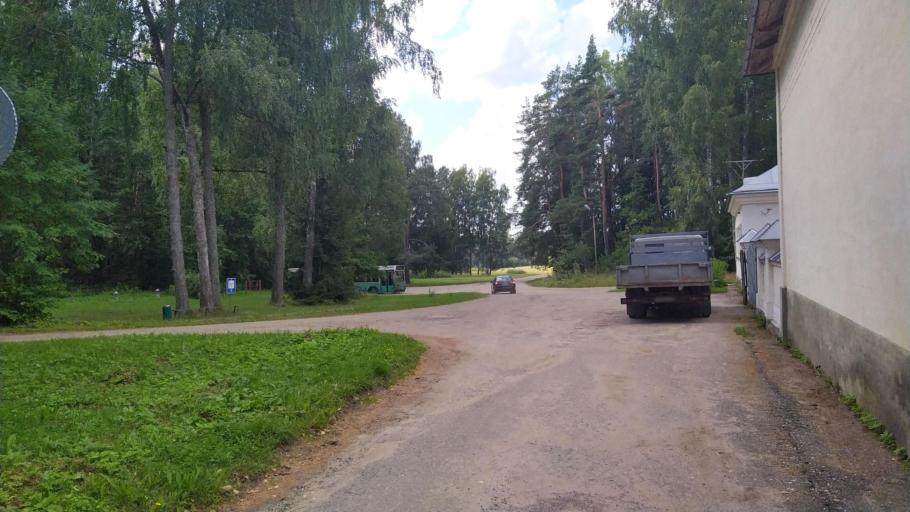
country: RU
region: Pskov
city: Pushkinskiye Gory
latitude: 57.0594
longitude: 28.9327
